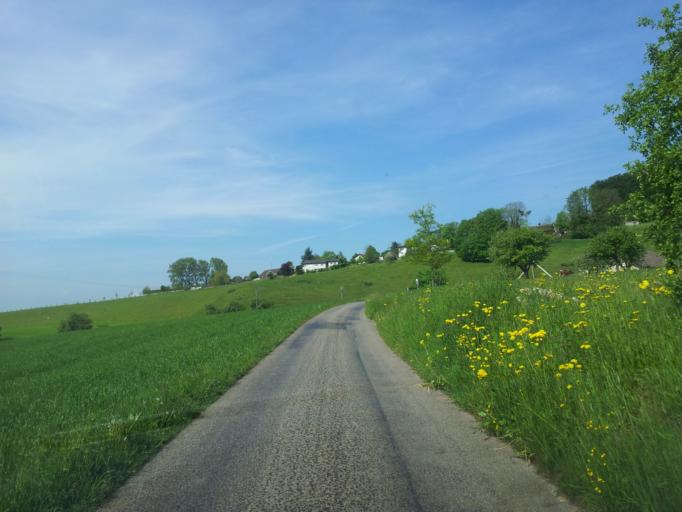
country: CH
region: Aargau
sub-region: Bezirk Bremgarten
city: Rudolfstetten
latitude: 47.3790
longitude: 8.3699
